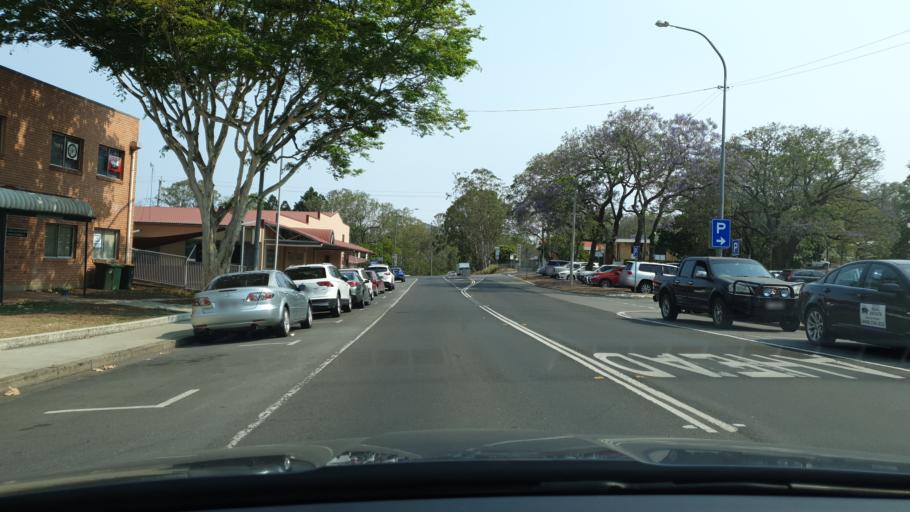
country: AU
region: Queensland
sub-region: Ipswich
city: Deebing Heights
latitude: -27.9978
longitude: 152.6815
